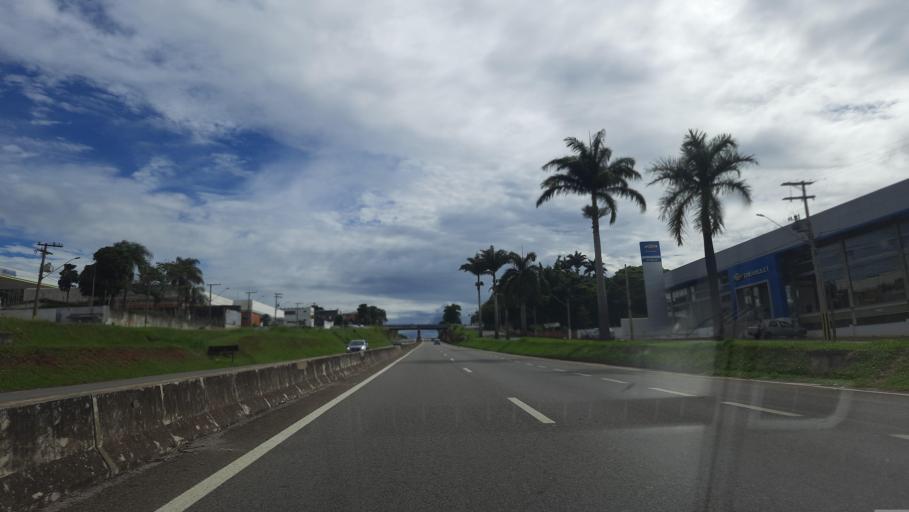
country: BR
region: Sao Paulo
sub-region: Sao Joao Da Boa Vista
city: Sao Joao da Boa Vista
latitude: -21.9826
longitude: -46.7870
